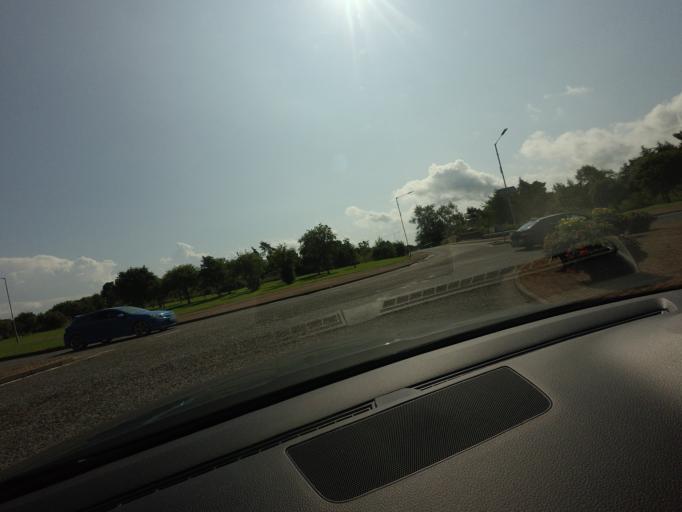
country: GB
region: Scotland
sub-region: Highland
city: Alness
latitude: 57.6927
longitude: -4.2708
